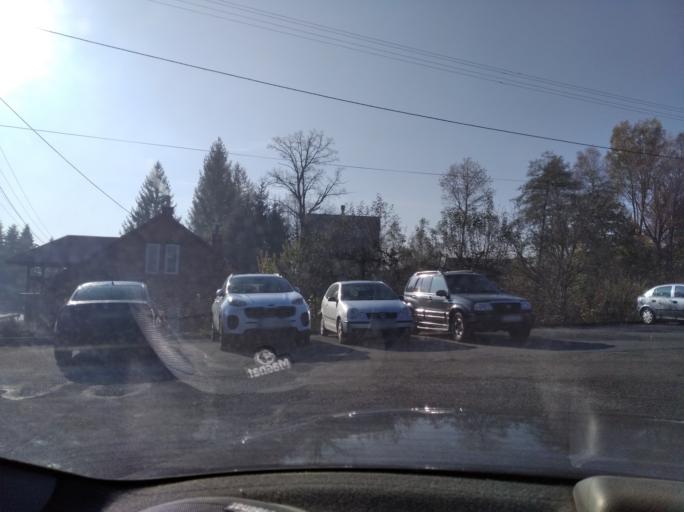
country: PL
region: Subcarpathian Voivodeship
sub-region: Powiat strzyzowski
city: Wysoka Strzyzowska
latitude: 49.8330
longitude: 21.7408
